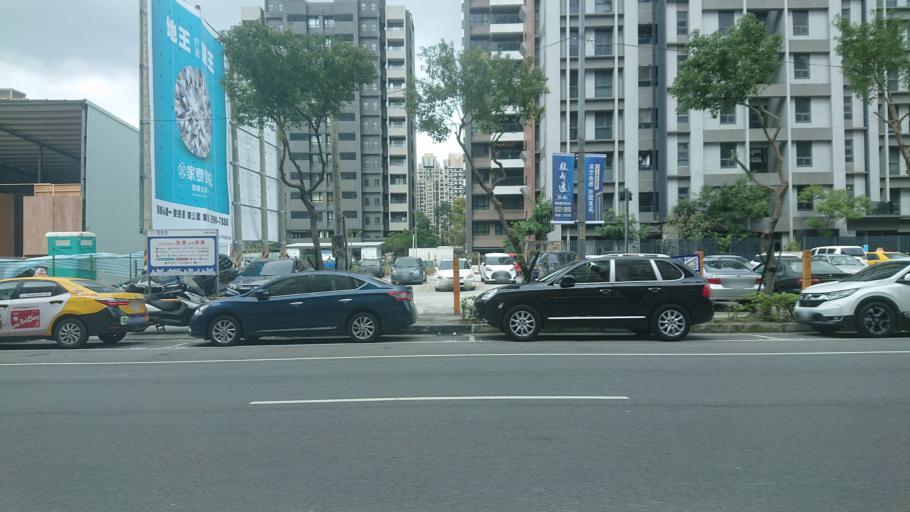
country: TW
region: Taipei
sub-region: Taipei
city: Banqiao
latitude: 25.0545
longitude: 121.4567
